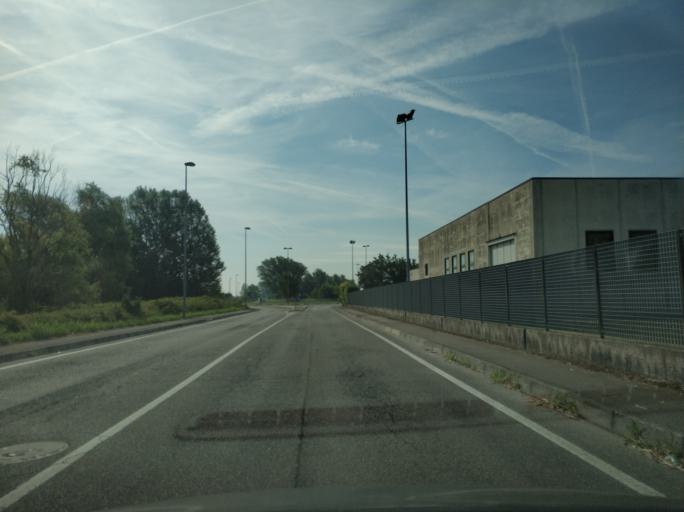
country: IT
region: Veneto
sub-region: Provincia di Padova
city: Este
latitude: 45.2149
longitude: 11.6791
